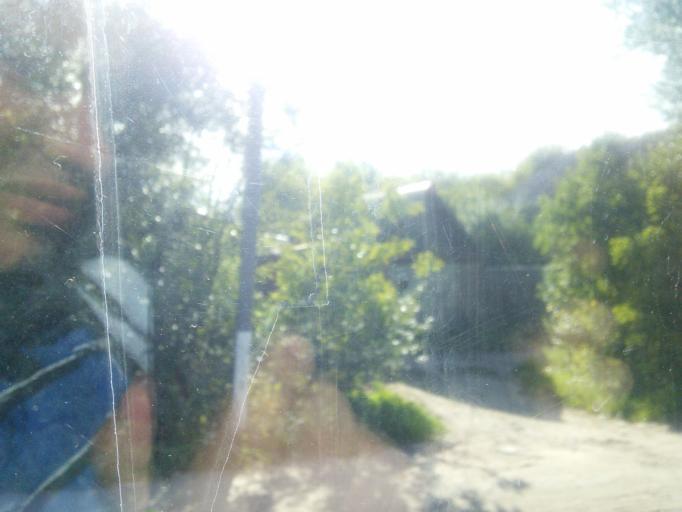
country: RU
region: Tverskaya
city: Bezhetsk
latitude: 57.7686
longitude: 36.7060
